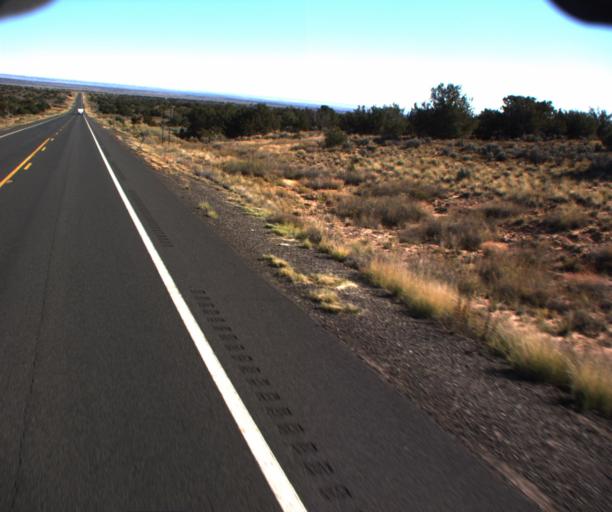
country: US
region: Arizona
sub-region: Apache County
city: Houck
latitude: 35.3438
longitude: -109.4506
